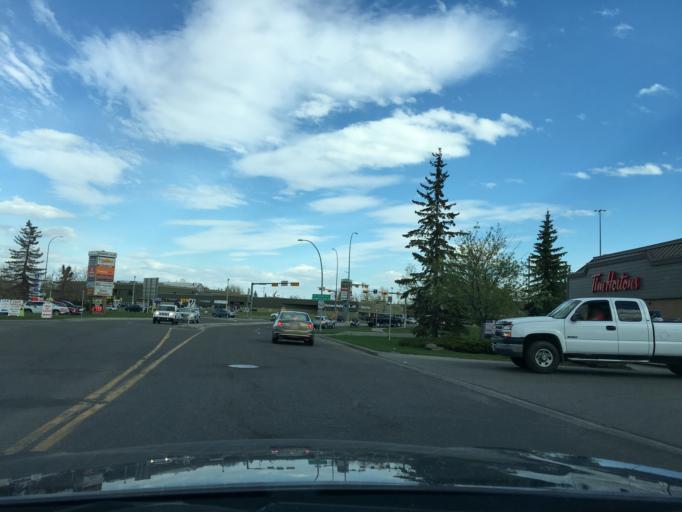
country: CA
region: Alberta
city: Calgary
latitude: 50.9148
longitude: -114.0660
